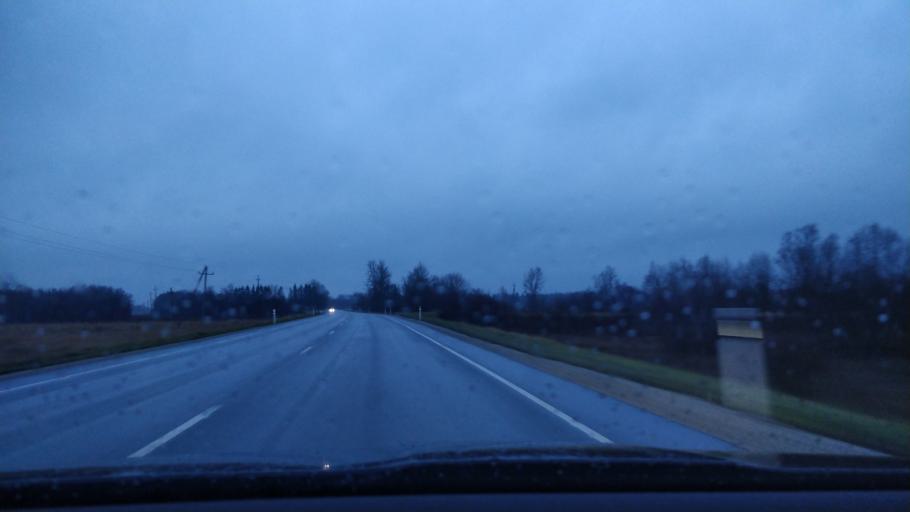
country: EE
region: Laeaene
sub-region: Lihula vald
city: Lihula
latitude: 58.8401
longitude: 24.0579
